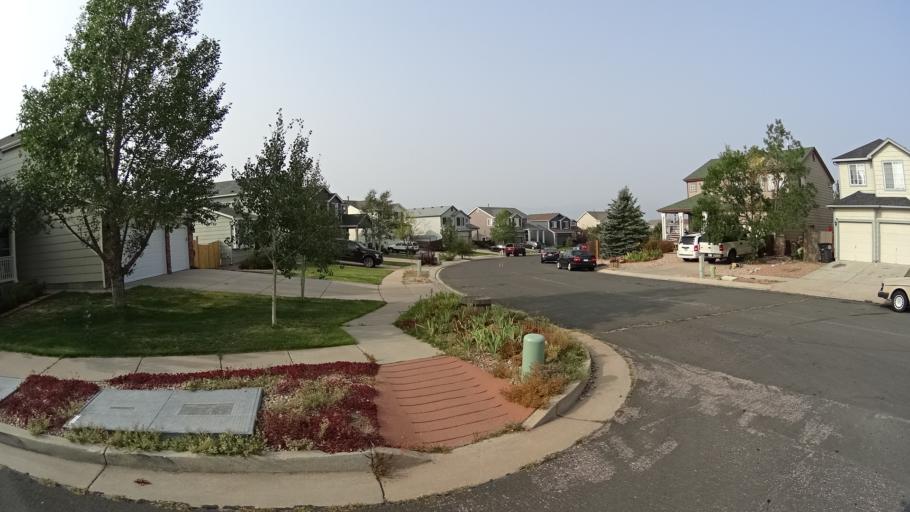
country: US
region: Colorado
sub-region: El Paso County
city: Cimarron Hills
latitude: 38.9321
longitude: -104.7305
